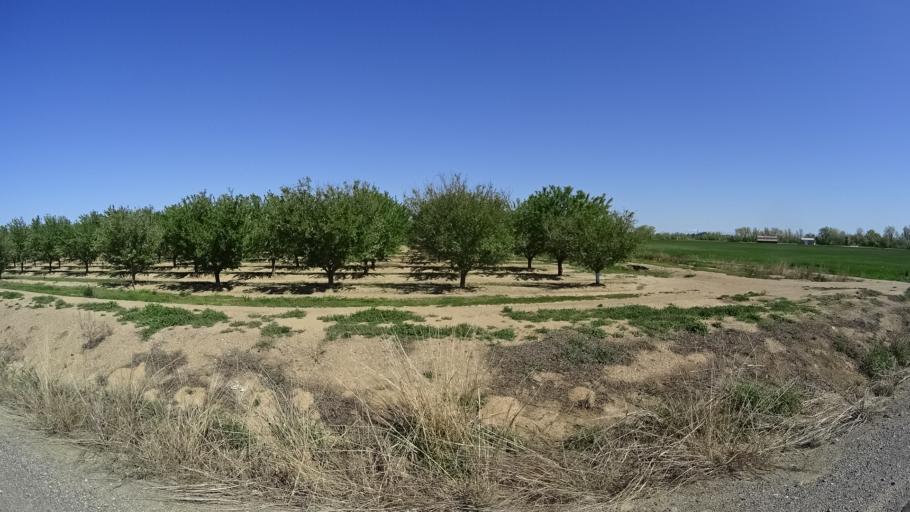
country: US
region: California
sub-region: Glenn County
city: Orland
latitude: 39.6972
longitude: -122.2334
